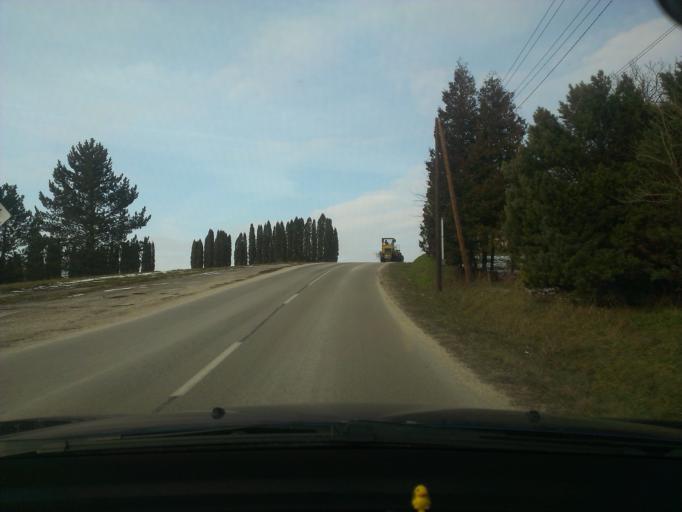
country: SK
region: Nitriansky
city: Stara Tura
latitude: 48.7069
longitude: 17.6842
